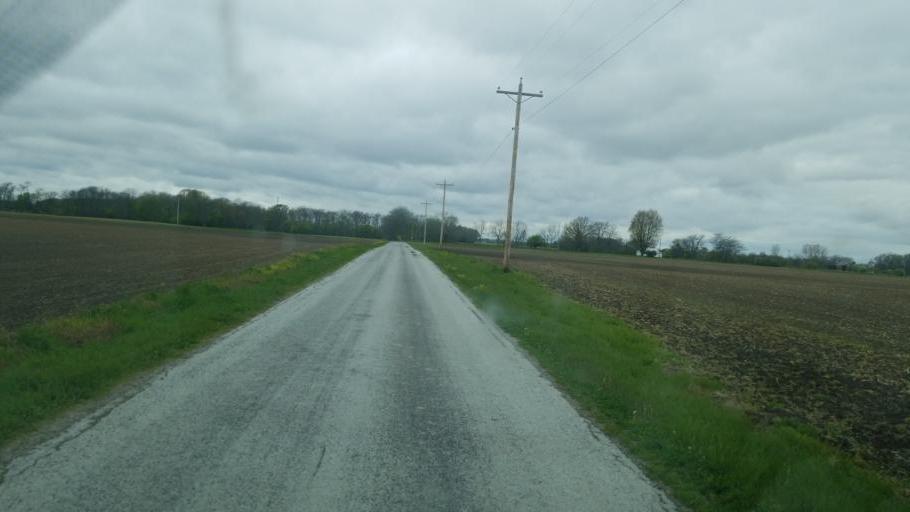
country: US
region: Ohio
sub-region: Hardin County
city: Kenton
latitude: 40.7246
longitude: -83.5860
